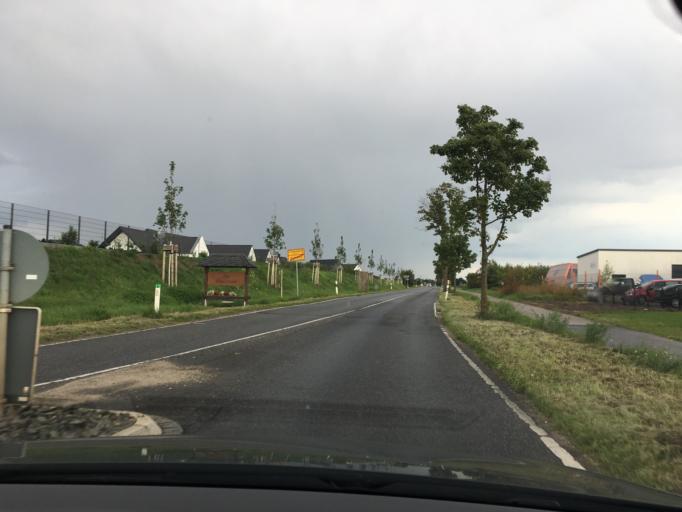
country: DE
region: North Rhine-Westphalia
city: Tuernich
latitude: 50.8332
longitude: 6.7495
